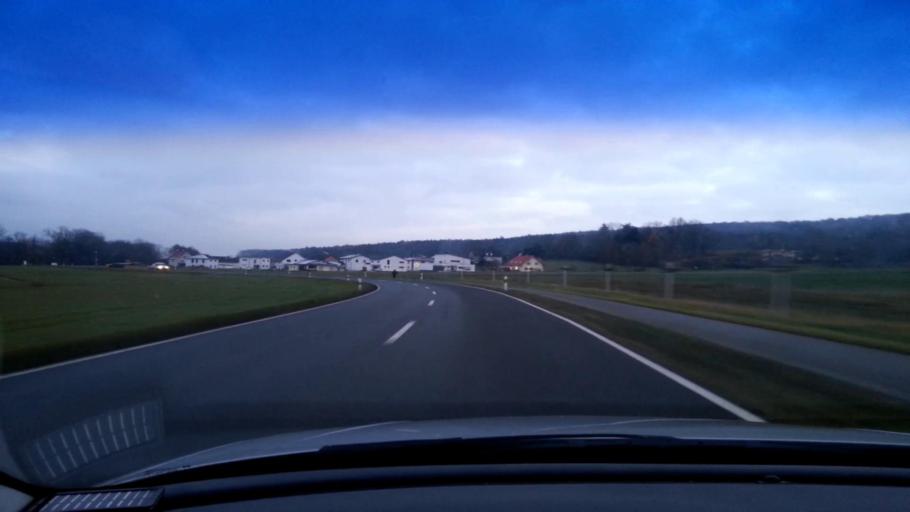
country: DE
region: Bavaria
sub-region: Upper Franconia
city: Frensdorf
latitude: 49.8493
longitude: 10.8879
